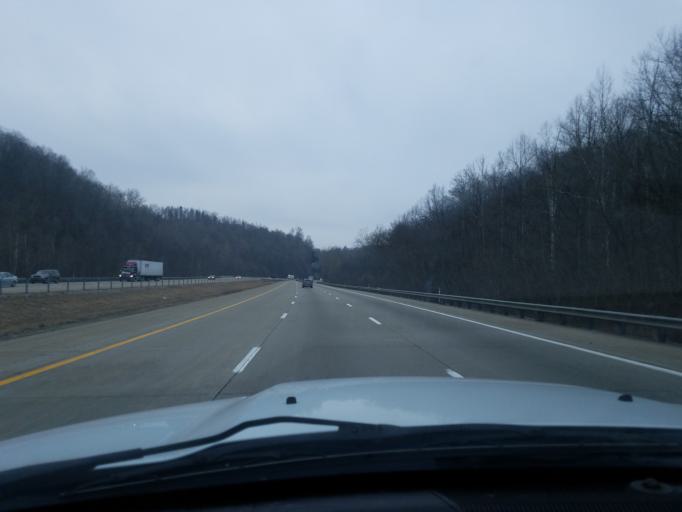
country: US
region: Kentucky
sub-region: Bullitt County
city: Lebanon Junction
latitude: 37.7666
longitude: -85.7929
